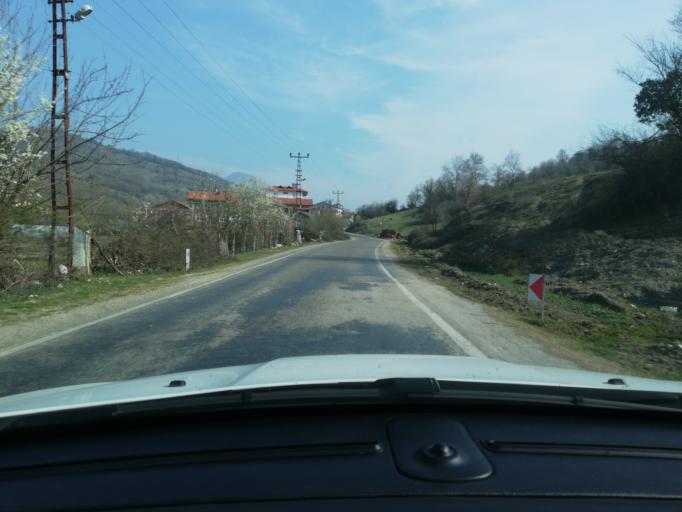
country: TR
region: Karabuk
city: Yenice
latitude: 41.2516
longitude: 32.3581
